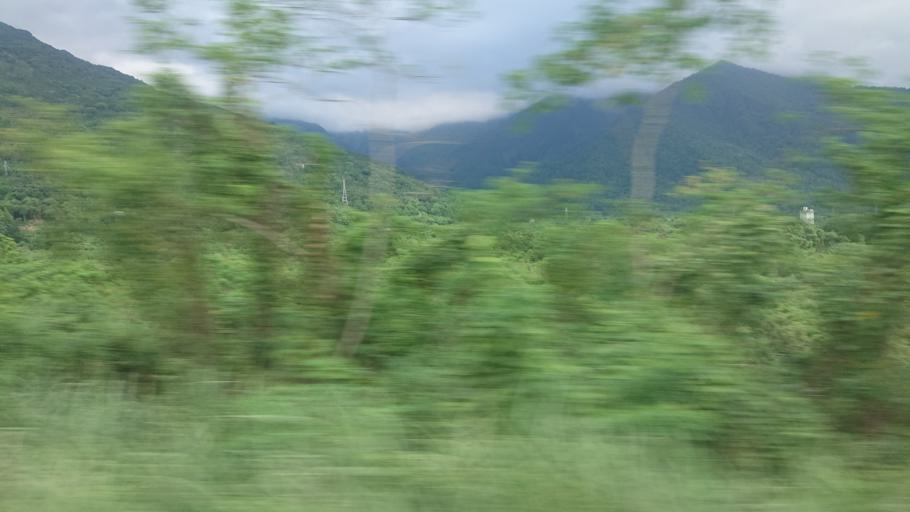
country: TW
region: Taiwan
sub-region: Hualien
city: Hualian
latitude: 23.6250
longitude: 121.3993
